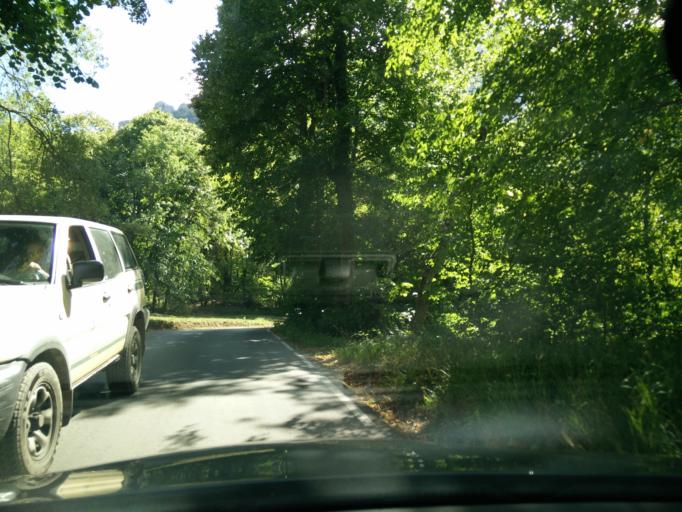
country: ES
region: Castille and Leon
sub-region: Provincia de Leon
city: Posada de Valdeon
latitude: 43.1923
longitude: -4.9089
